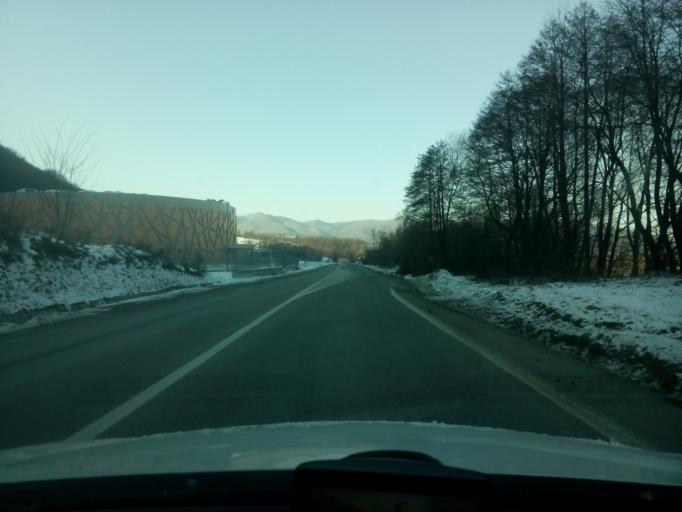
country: RO
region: Valcea
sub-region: Comuna Daesti
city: Daesti
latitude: 45.2105
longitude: 24.3658
